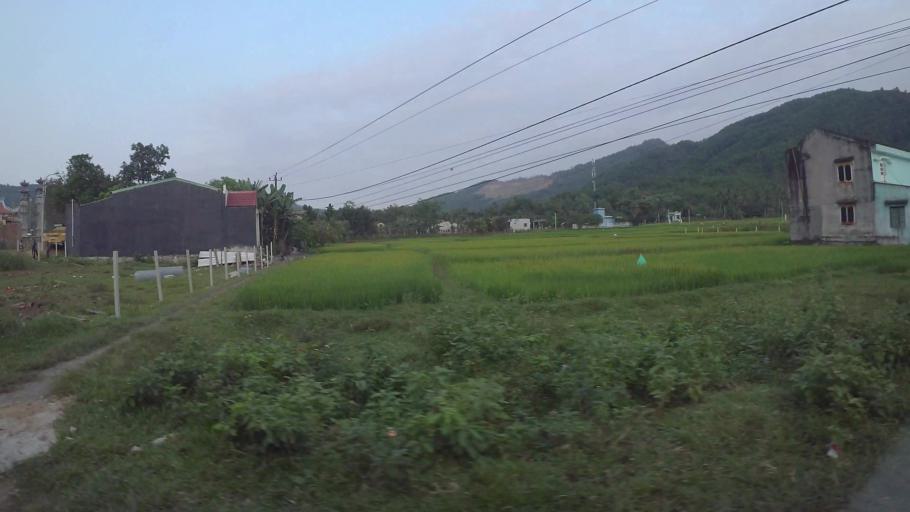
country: VN
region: Da Nang
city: Lien Chieu
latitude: 16.0542
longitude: 108.1140
